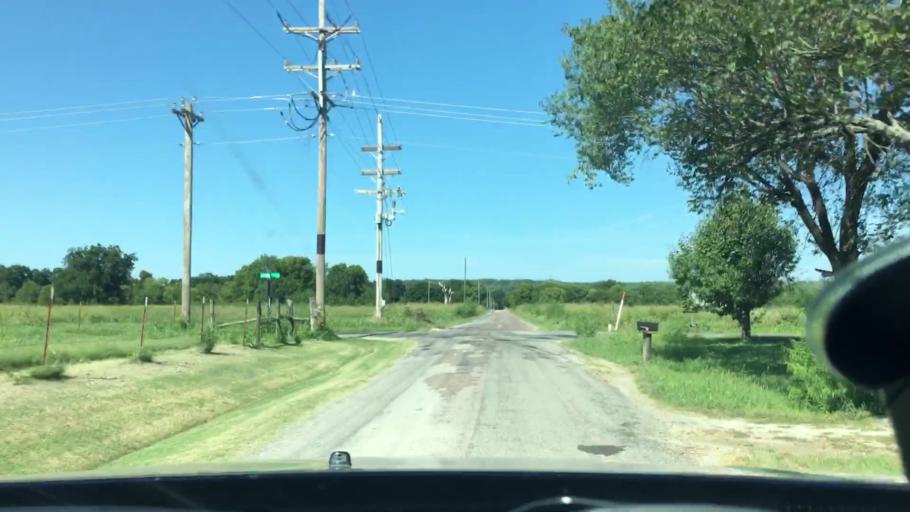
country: US
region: Oklahoma
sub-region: Pontotoc County
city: Ada
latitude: 34.7236
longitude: -96.6520
